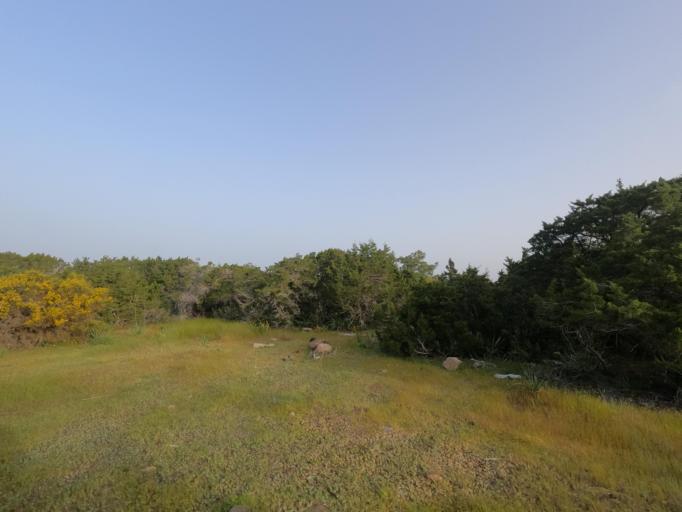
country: CY
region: Pafos
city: Pegeia
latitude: 34.9765
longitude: 32.3164
